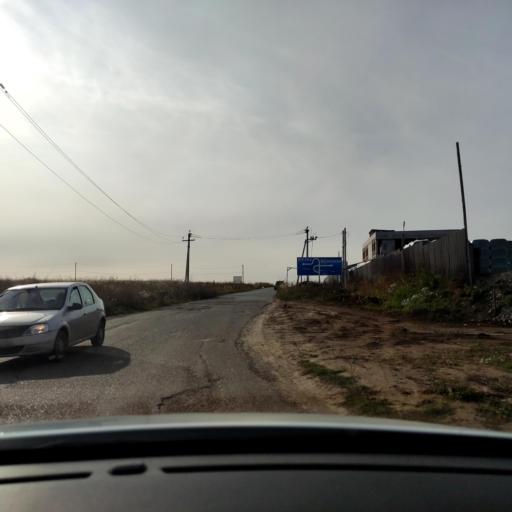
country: RU
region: Tatarstan
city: Vysokaya Gora
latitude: 55.8527
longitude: 49.3386
